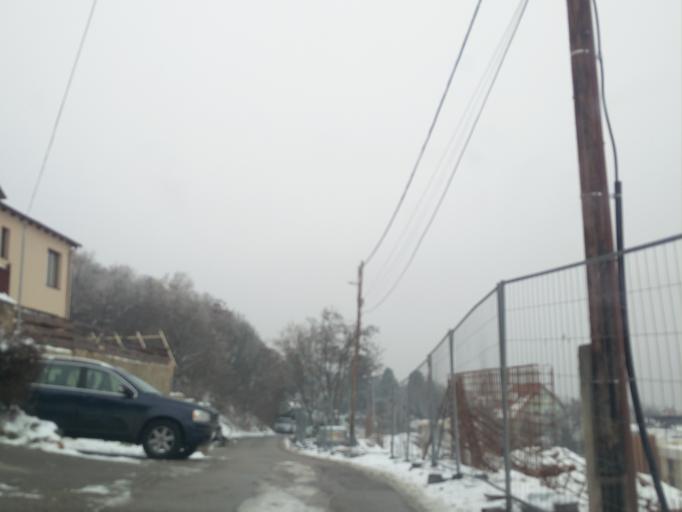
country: HU
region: Budapest
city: Budapest III. keruelet
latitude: 47.5413
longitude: 19.0199
